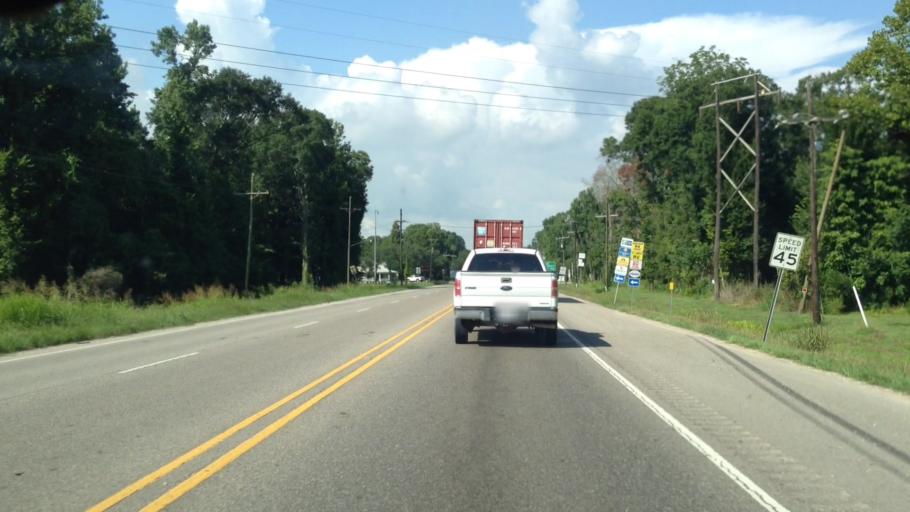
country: US
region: Louisiana
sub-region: Ascension Parish
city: Sorrento
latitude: 30.1685
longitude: -90.8796
